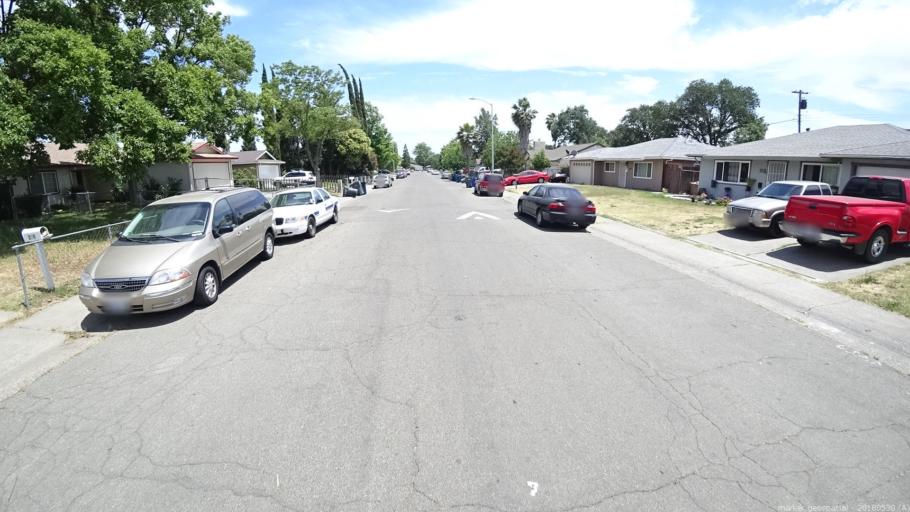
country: US
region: California
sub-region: Sacramento County
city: Sacramento
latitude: 38.6279
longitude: -121.4609
